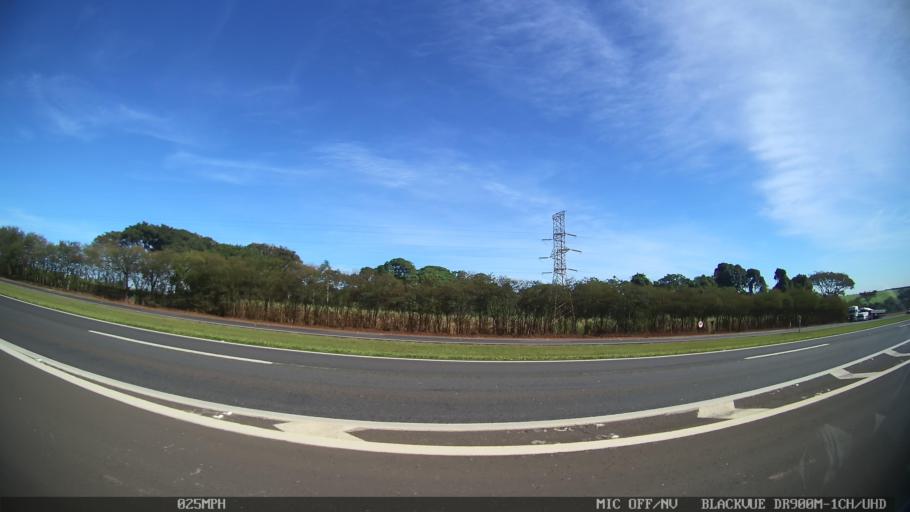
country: BR
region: Sao Paulo
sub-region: Araras
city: Araras
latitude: -22.3151
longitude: -47.3906
